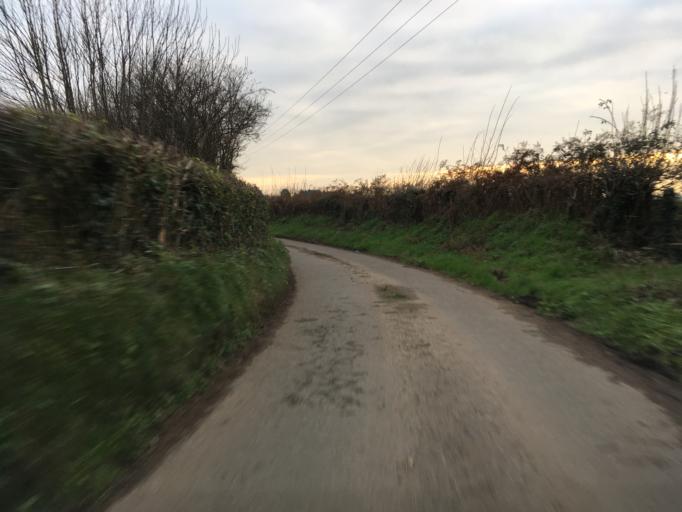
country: GB
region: Wales
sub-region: Newport
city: Marshfield
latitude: 51.5426
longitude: -3.0933
